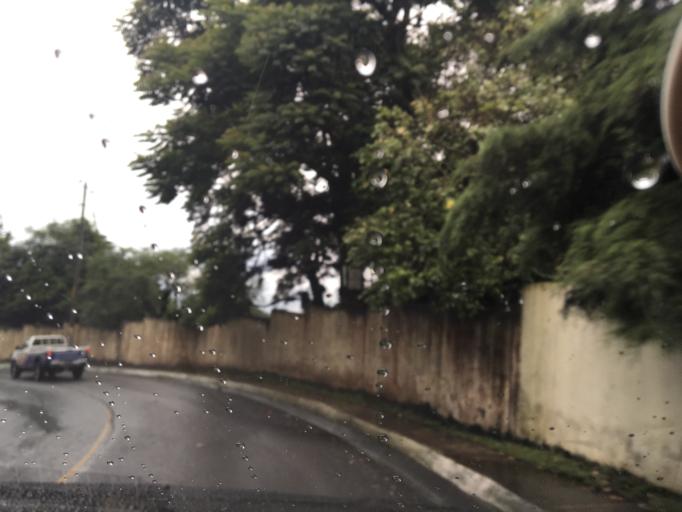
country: GT
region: Guatemala
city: Santa Catarina Pinula
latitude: 14.5532
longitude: -90.4946
